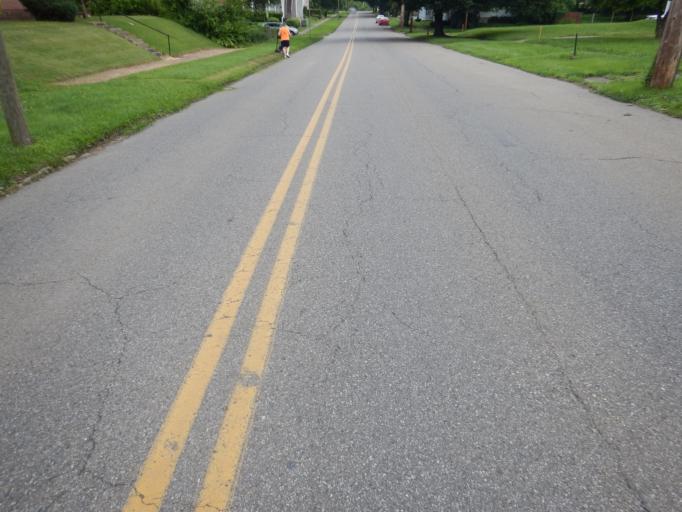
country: US
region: Ohio
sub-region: Muskingum County
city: Zanesville
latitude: 39.9308
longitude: -82.0056
